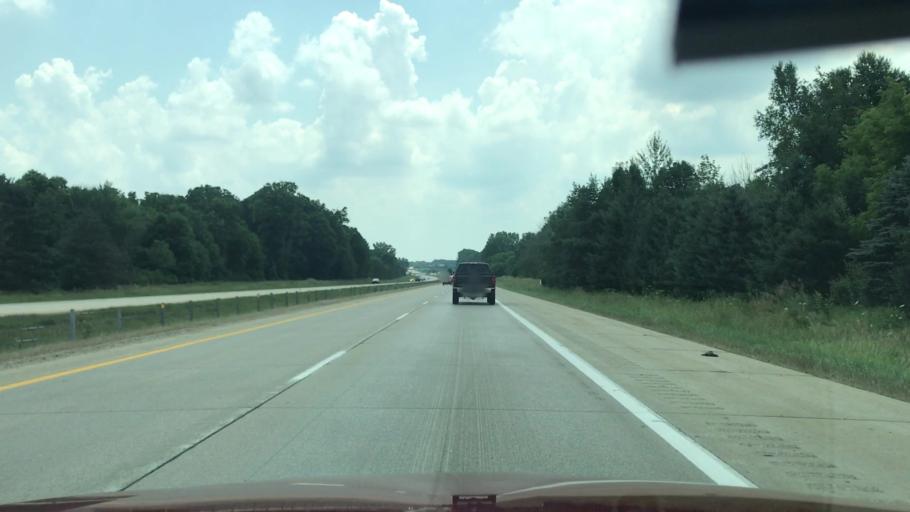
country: US
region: Michigan
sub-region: Allegan County
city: Plainwell
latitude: 42.4779
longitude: -85.6529
